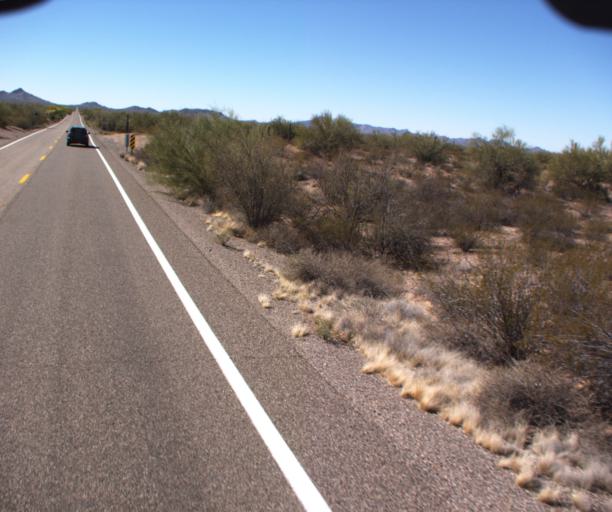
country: US
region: Arizona
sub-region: Pima County
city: Ajo
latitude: 32.1559
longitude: -112.7646
